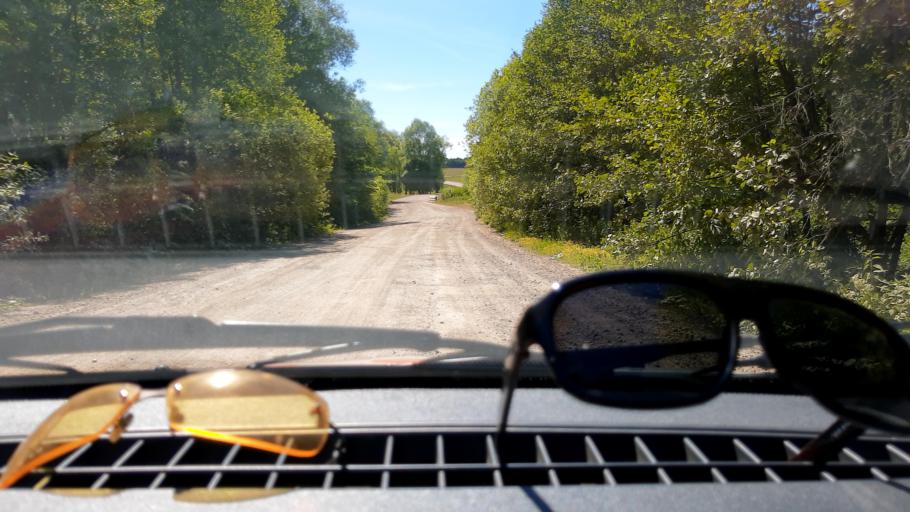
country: RU
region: Bashkortostan
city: Ulu-Telyak
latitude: 54.7973
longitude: 57.0152
